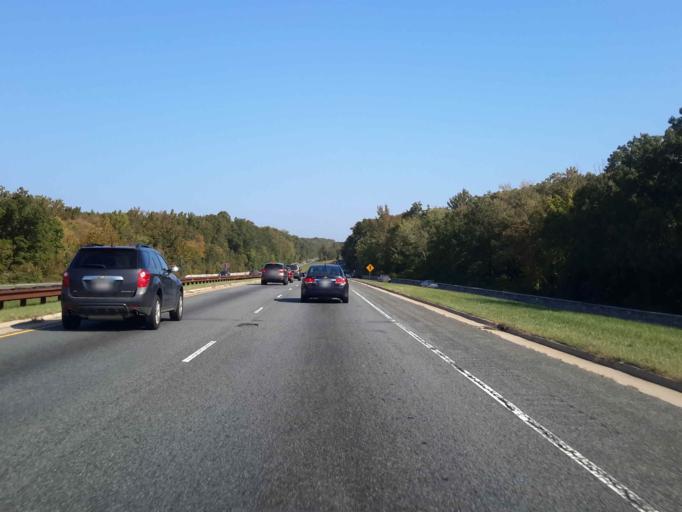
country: US
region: Maryland
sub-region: Prince George's County
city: South Laurel
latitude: 39.0342
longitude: -76.8515
